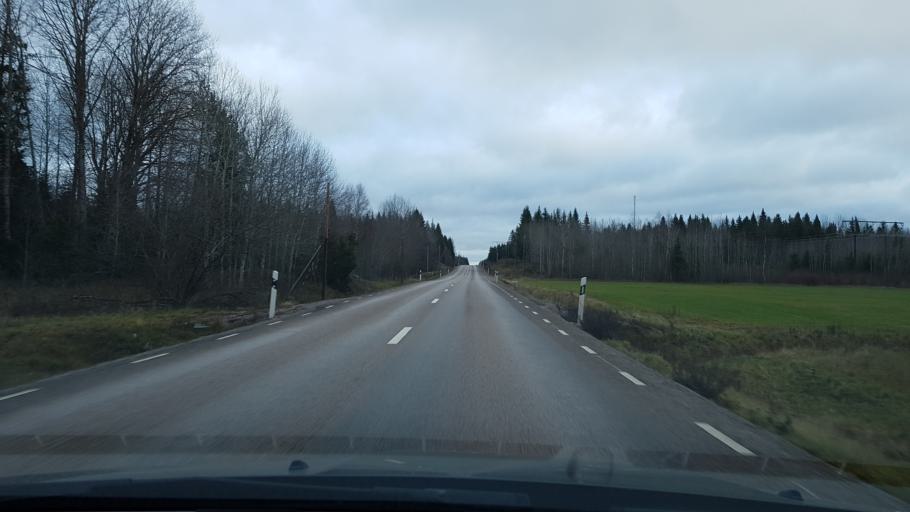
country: SE
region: Uppsala
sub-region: Osthammars Kommun
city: Gimo
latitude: 59.9815
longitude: 18.2004
